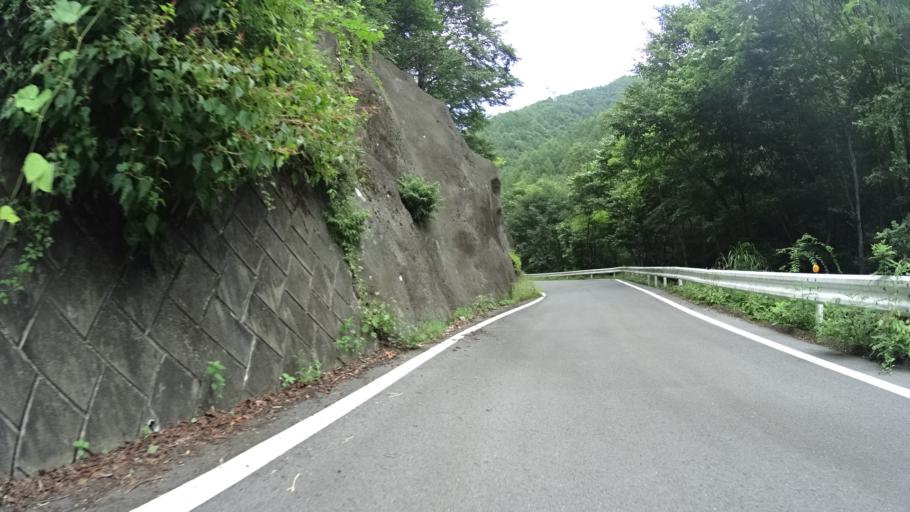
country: JP
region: Nagano
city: Saku
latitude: 36.0674
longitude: 138.6683
